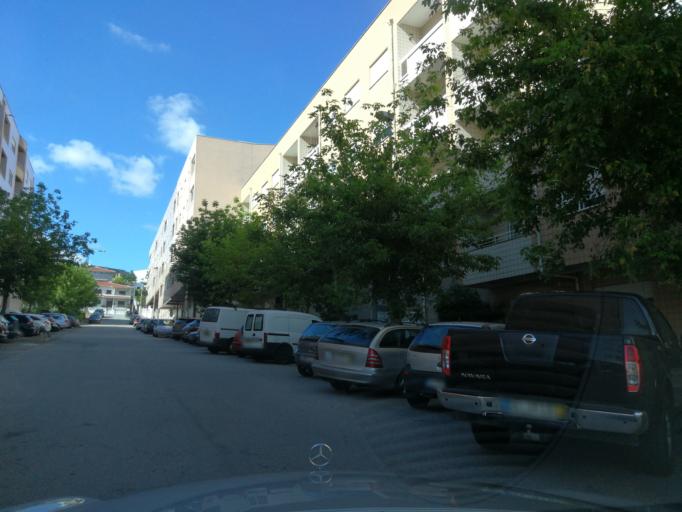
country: PT
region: Braga
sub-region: Braga
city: Adaufe
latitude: 41.5681
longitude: -8.3855
